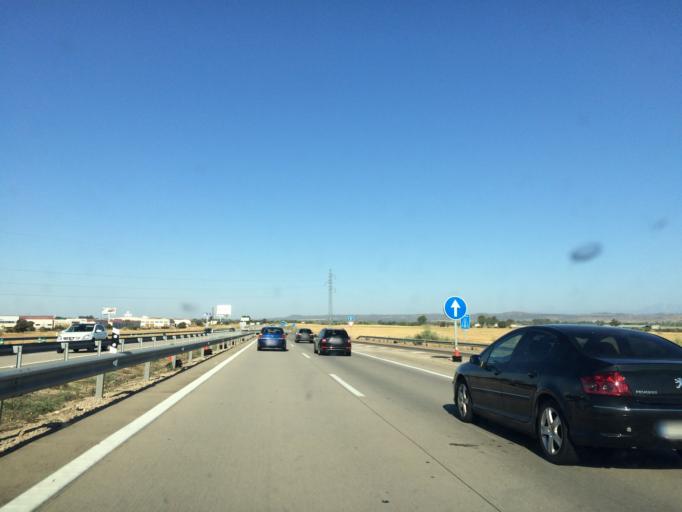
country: ES
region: Castille-La Mancha
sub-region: Province of Toledo
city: Cazalegas
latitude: 39.9818
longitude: -4.7316
